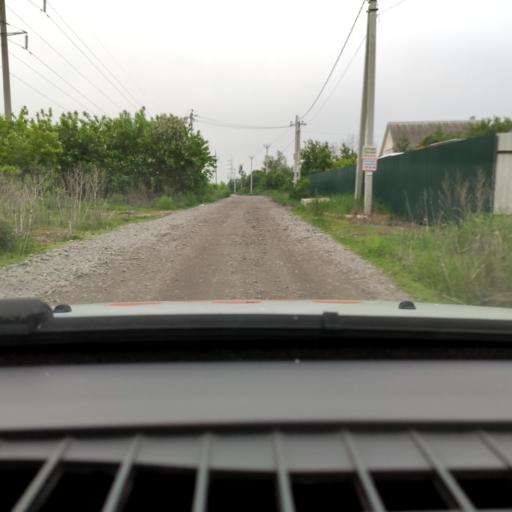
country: RU
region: Voronezj
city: Novaya Usman'
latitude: 51.6609
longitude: 39.4108
